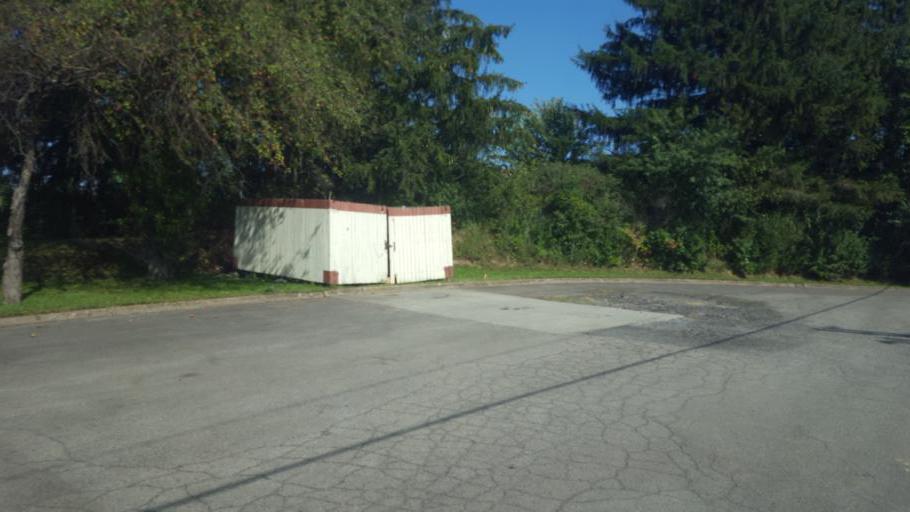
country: US
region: Pennsylvania
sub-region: Clarion County
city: Clarion
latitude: 41.1896
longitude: -79.3912
